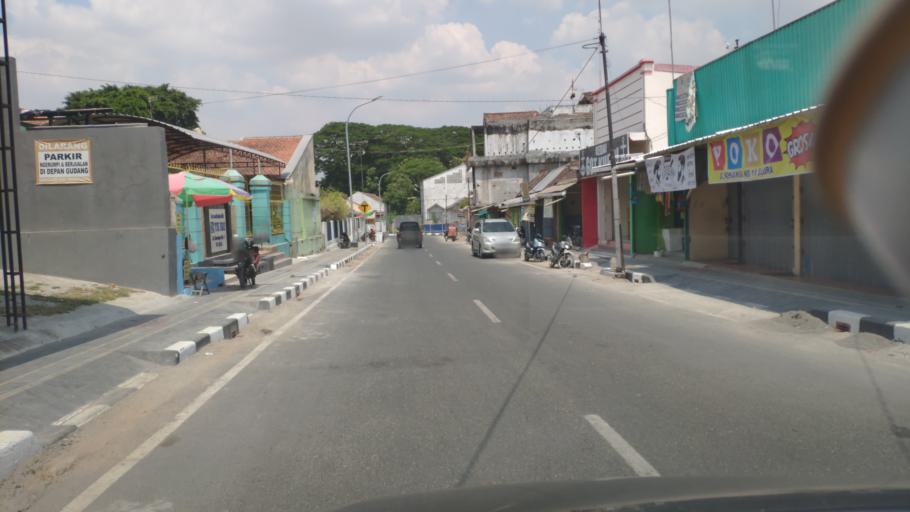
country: ID
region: Central Java
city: Mlangsen
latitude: -6.9702
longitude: 111.4130
